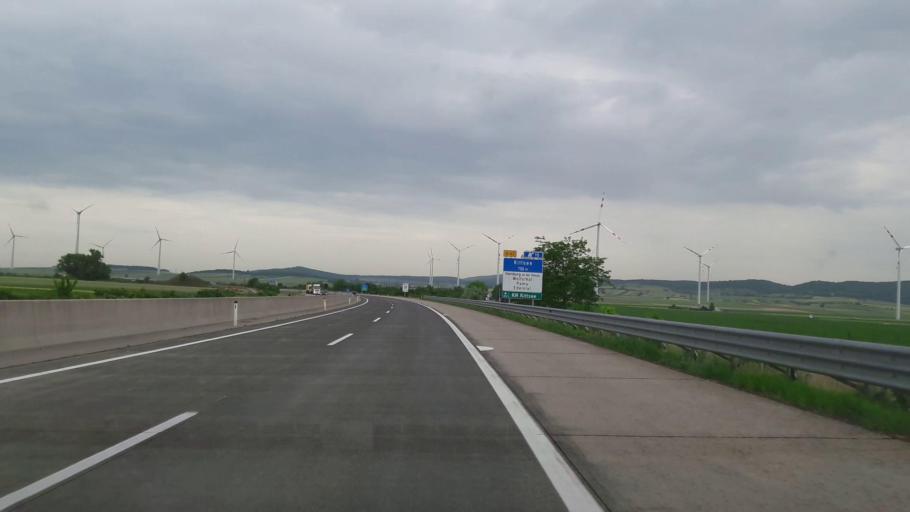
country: AT
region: Burgenland
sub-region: Politischer Bezirk Neusiedl am See
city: Kittsee
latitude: 48.0808
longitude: 17.0472
